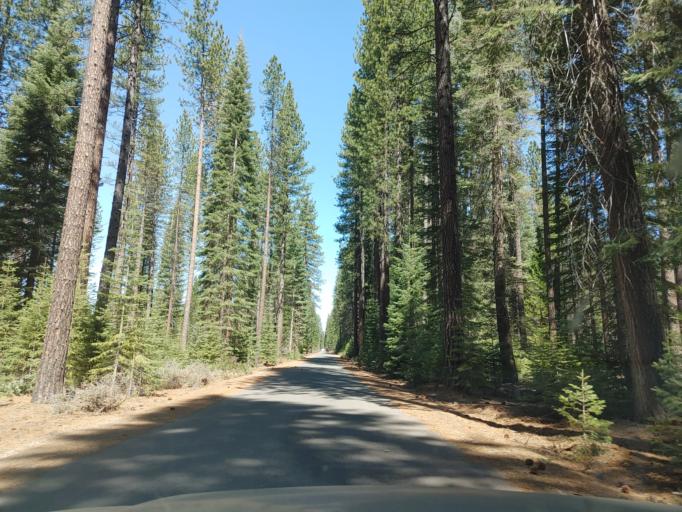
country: US
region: California
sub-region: Siskiyou County
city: McCloud
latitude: 41.2588
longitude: -121.9427
